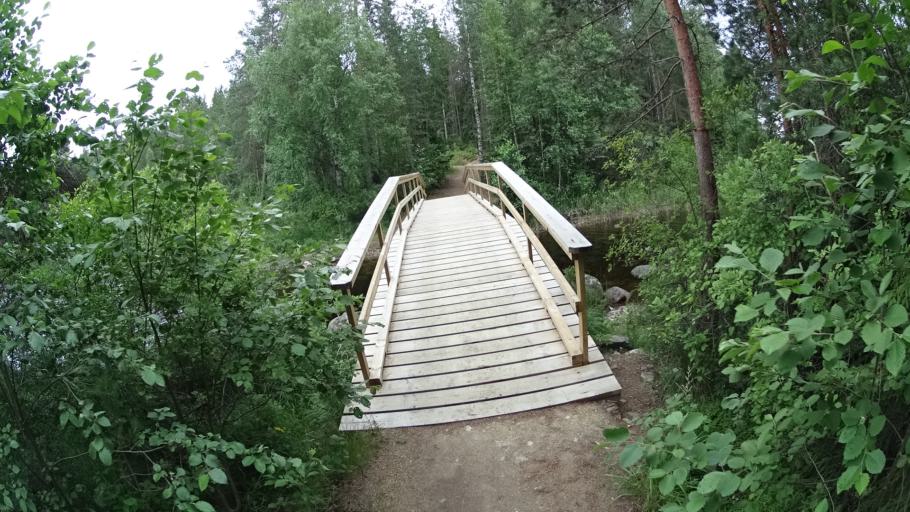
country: FI
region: Southern Savonia
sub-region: Mikkeli
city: Maentyharju
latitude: 61.1778
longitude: 26.8962
